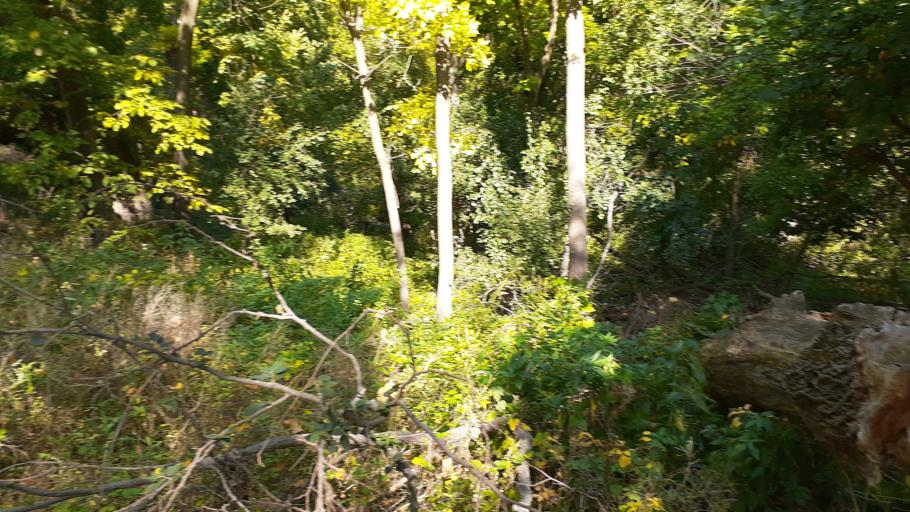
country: US
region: Minnesota
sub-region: Clay County
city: Oakport
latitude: 46.9182
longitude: -96.7612
